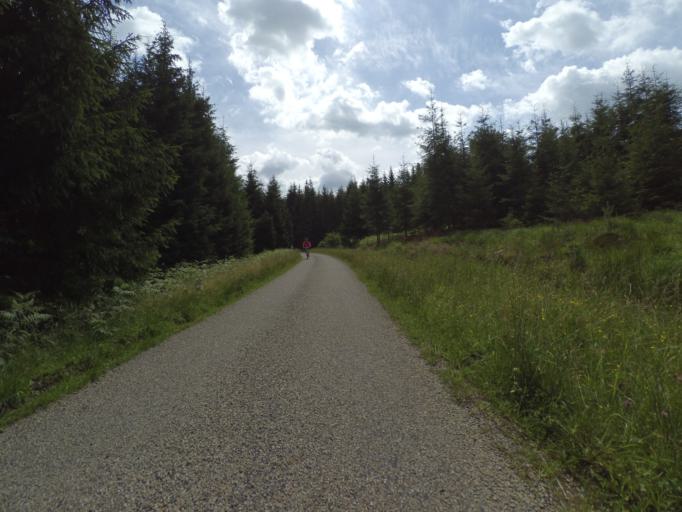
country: BE
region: Wallonia
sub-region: Province de Liege
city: Raeren
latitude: 50.5935
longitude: 6.1342
